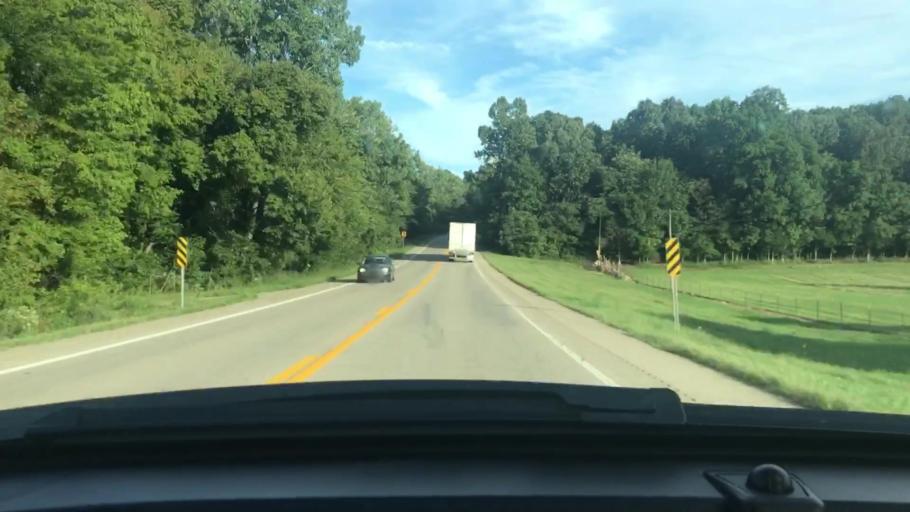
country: US
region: Arkansas
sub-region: Randolph County
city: Pocahontas
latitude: 36.2177
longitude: -91.2185
